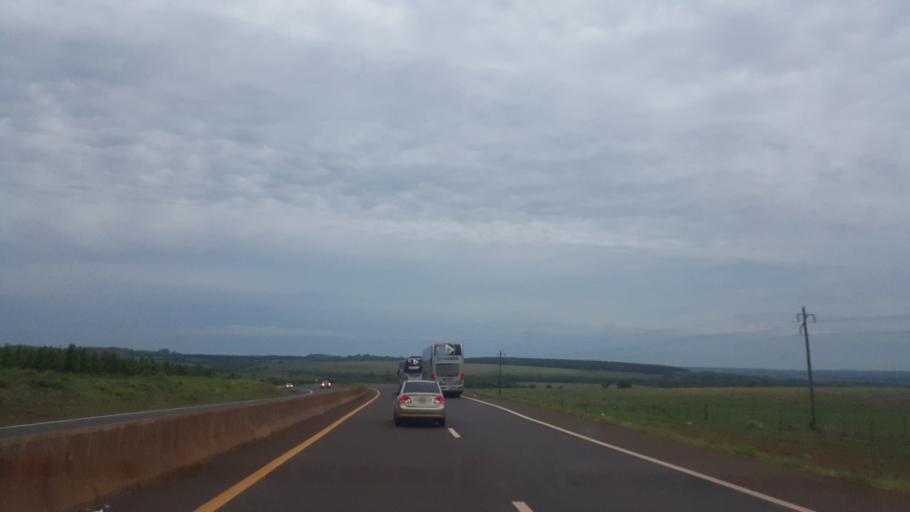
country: AR
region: Misiones
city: Garupa
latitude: -27.5690
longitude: -55.8452
